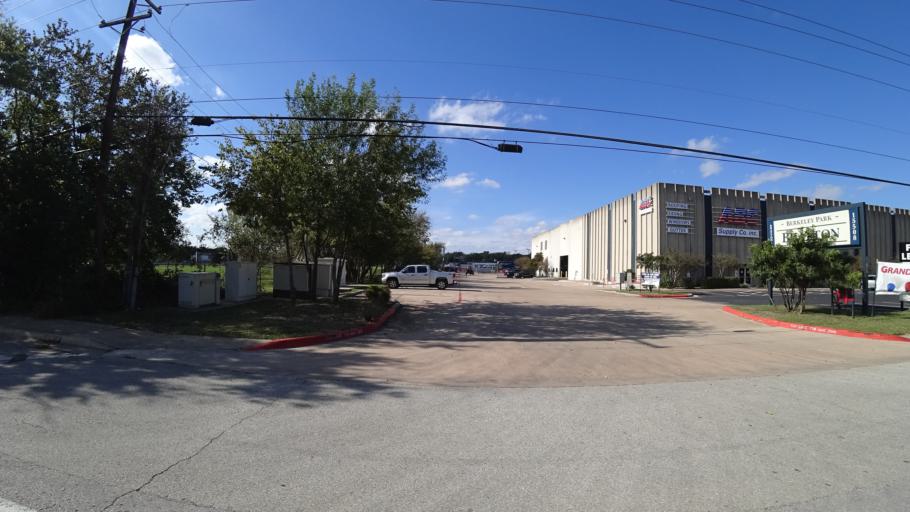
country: US
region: Texas
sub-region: Travis County
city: Wells Branch
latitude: 30.4563
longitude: -97.6786
